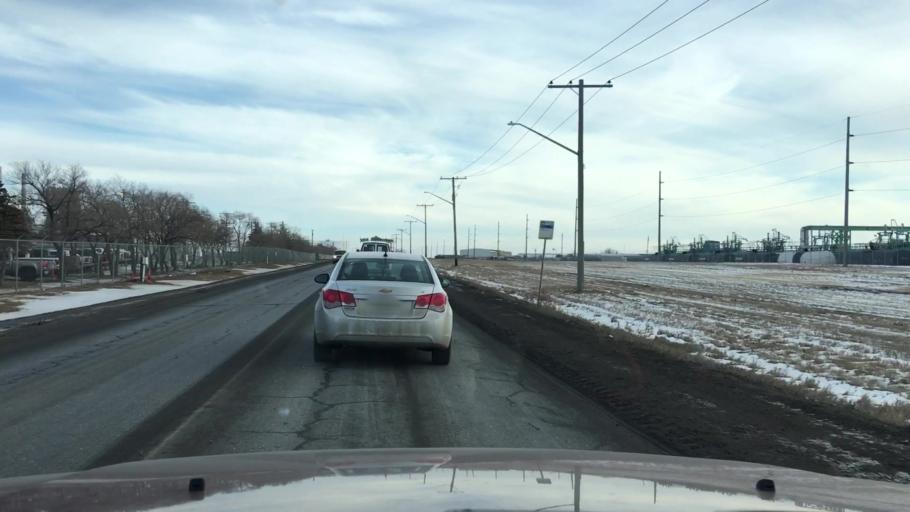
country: CA
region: Saskatchewan
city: Regina
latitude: 50.4825
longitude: -104.5786
